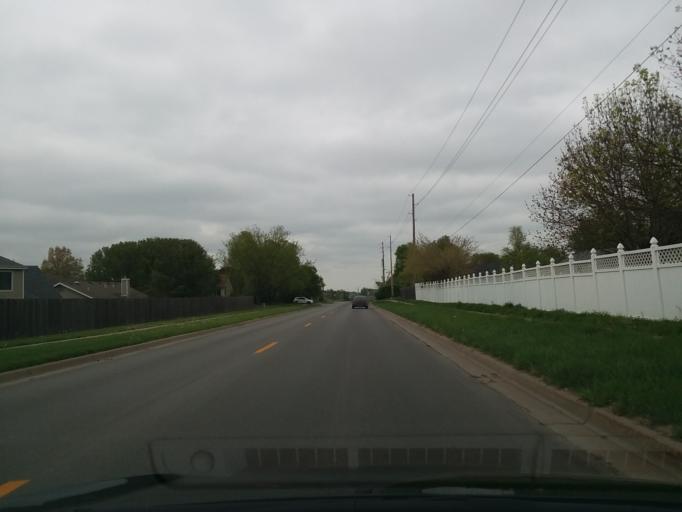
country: US
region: Kansas
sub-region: Douglas County
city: Lawrence
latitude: 38.9773
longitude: -95.2882
